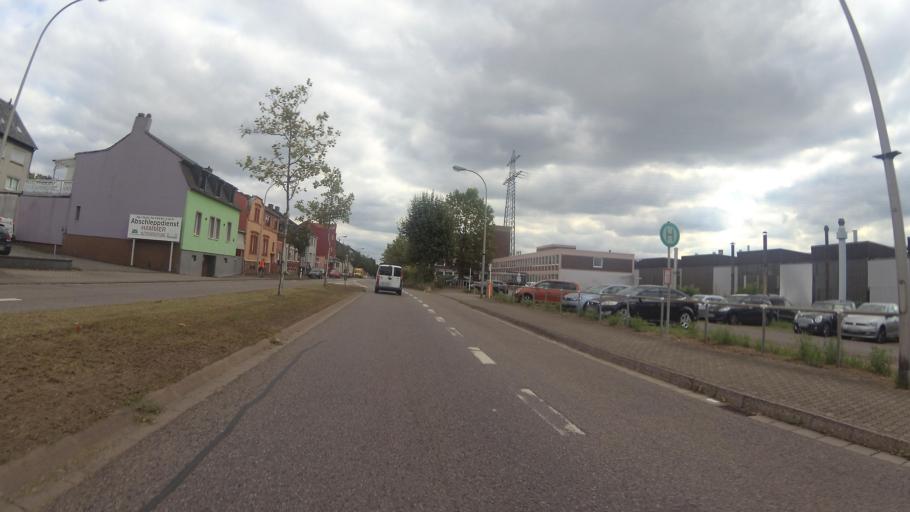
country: DE
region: Saarland
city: Volklingen
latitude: 49.2560
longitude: 6.8468
